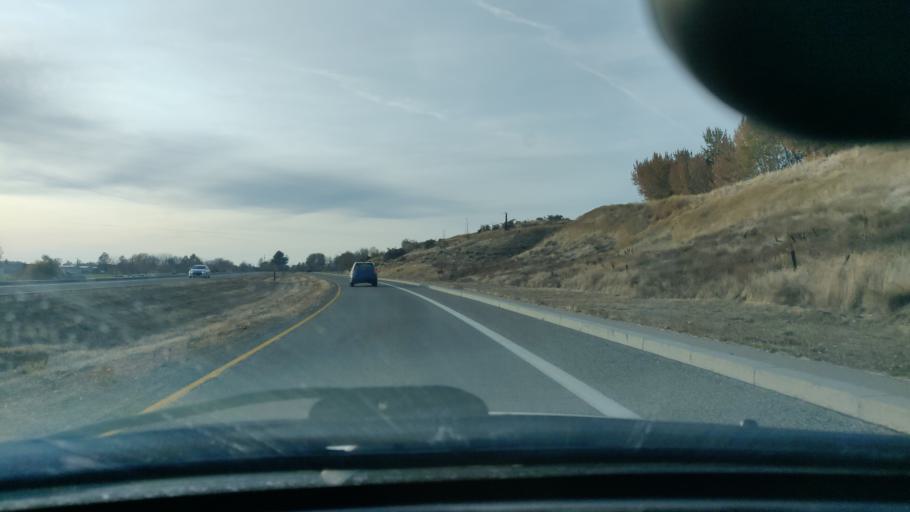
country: US
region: Idaho
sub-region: Ada County
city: Eagle
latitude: 43.6913
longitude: -116.3071
